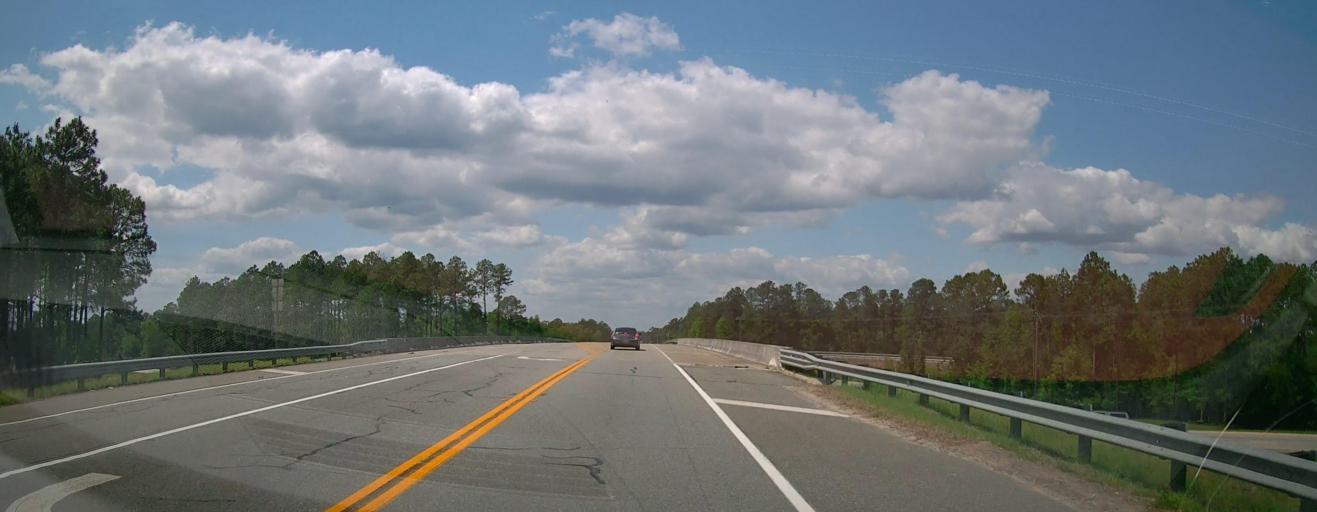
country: US
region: Georgia
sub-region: Treutlen County
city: Soperton
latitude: 32.4374
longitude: -82.6793
